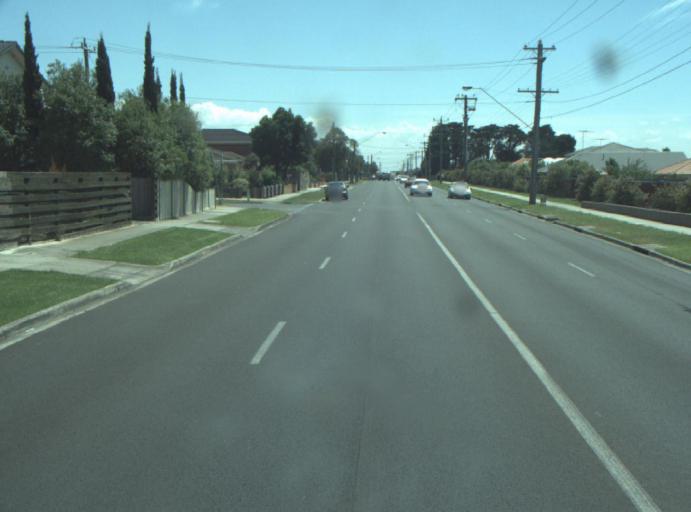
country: AU
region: Victoria
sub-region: Greater Geelong
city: Bell Park
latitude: -38.1019
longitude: 144.3332
